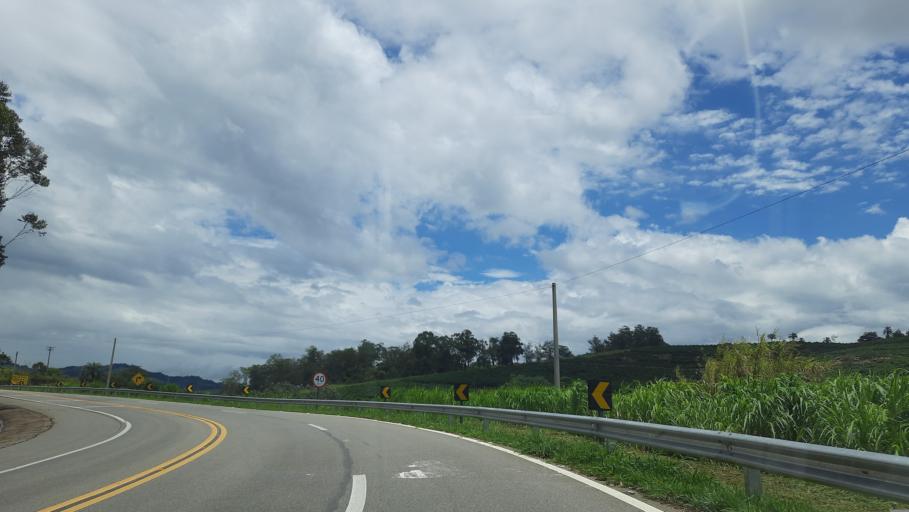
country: BR
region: Sao Paulo
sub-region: Vargem Grande Do Sul
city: Vargem Grande do Sul
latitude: -21.7998
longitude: -46.8201
